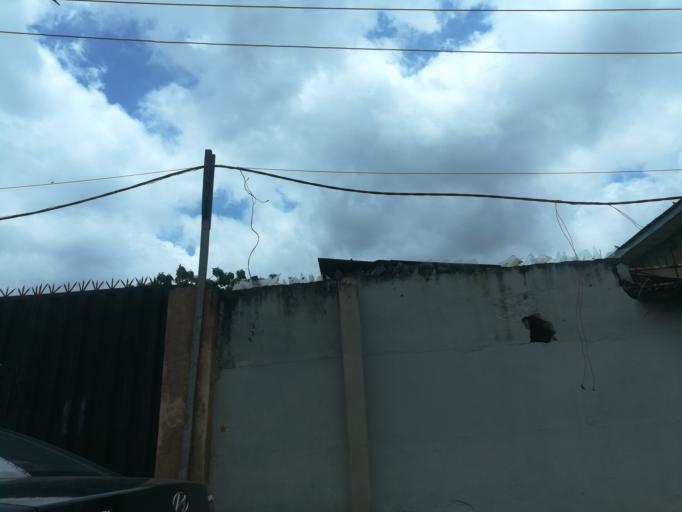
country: NG
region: Lagos
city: Somolu
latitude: 6.5553
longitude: 3.3655
